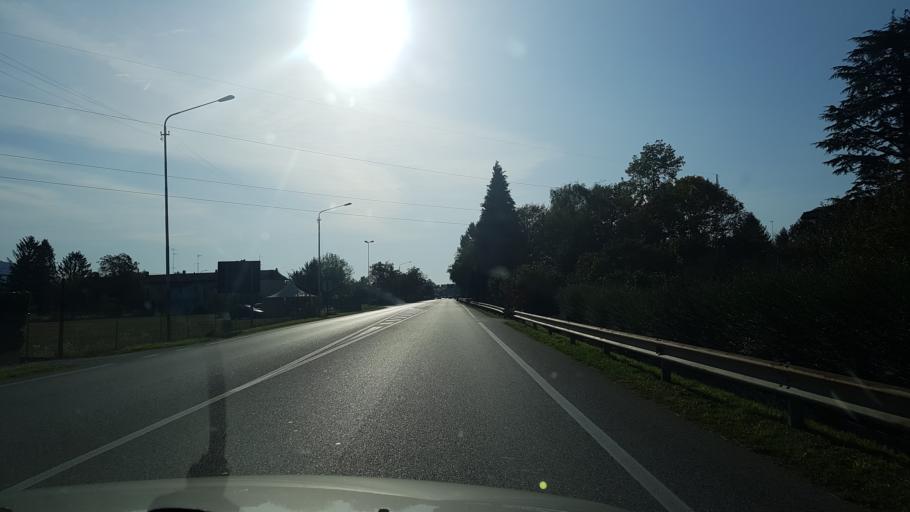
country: IT
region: Friuli Venezia Giulia
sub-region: Provincia di Udine
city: Gemona
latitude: 46.2557
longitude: 13.1122
